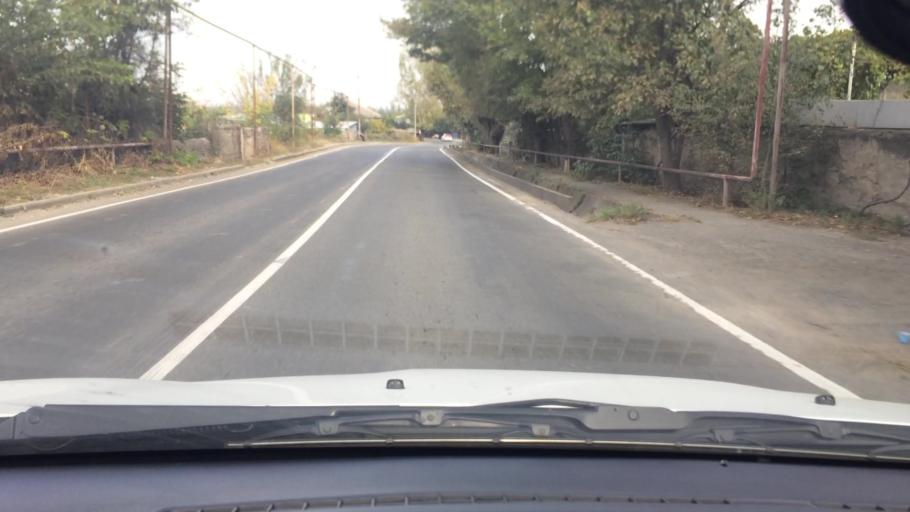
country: GE
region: Kvemo Kartli
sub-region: Marneuli
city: Marneuli
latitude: 41.4010
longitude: 44.8261
